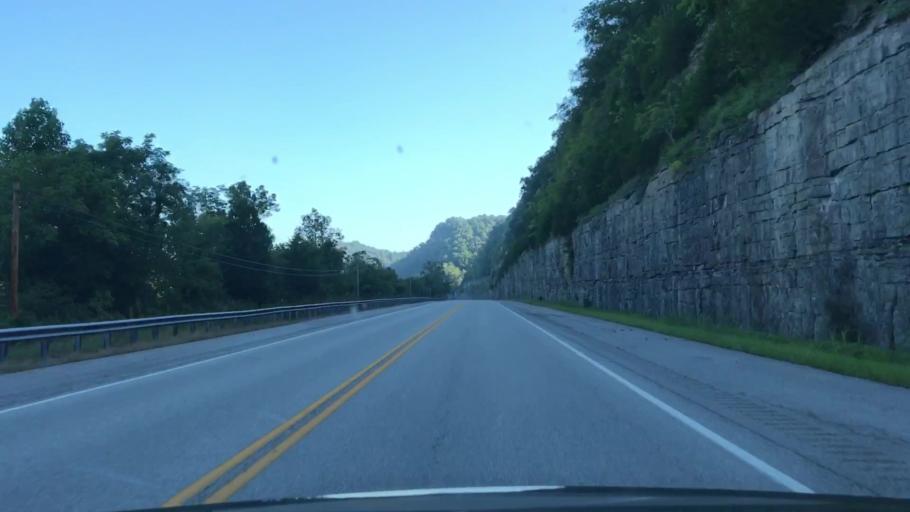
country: US
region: Tennessee
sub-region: Clay County
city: Celina
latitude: 36.4501
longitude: -85.5777
